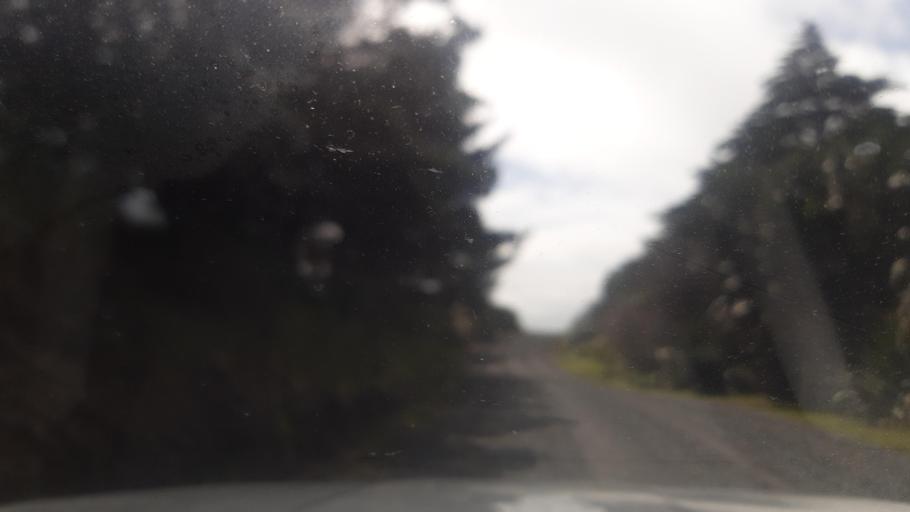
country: NZ
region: Northland
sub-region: Far North District
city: Kaitaia
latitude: -34.7415
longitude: 173.1142
